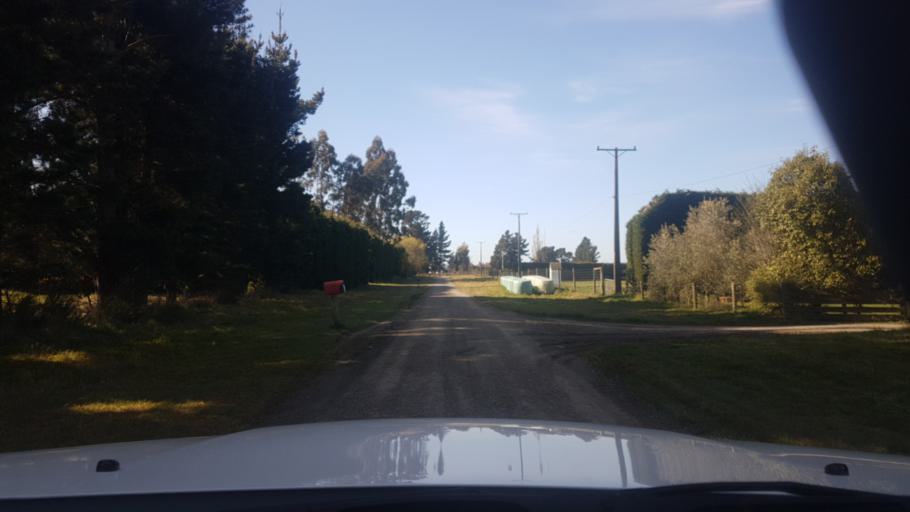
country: NZ
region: Canterbury
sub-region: Timaru District
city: Pleasant Point
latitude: -44.1465
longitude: 171.2879
